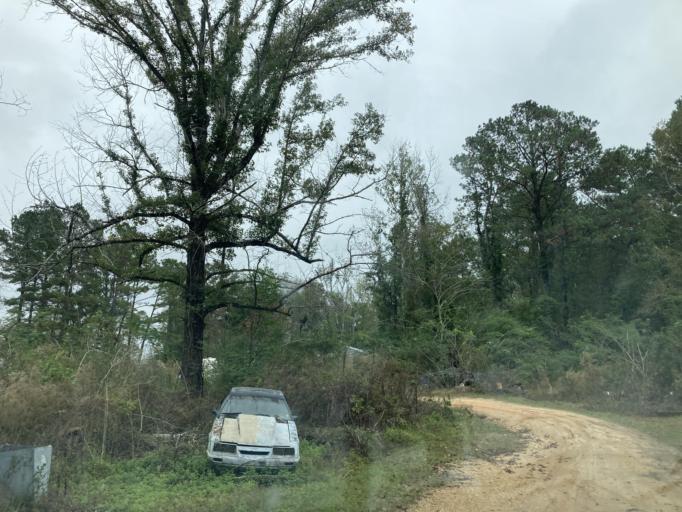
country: US
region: Mississippi
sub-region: Lamar County
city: West Hattiesburg
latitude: 31.2563
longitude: -89.5014
